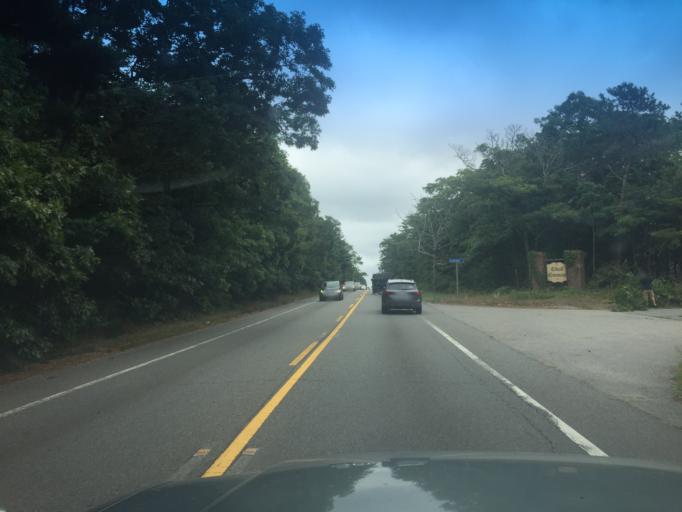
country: US
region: Massachusetts
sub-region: Barnstable County
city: Marstons Mills
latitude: 41.6440
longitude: -70.4361
